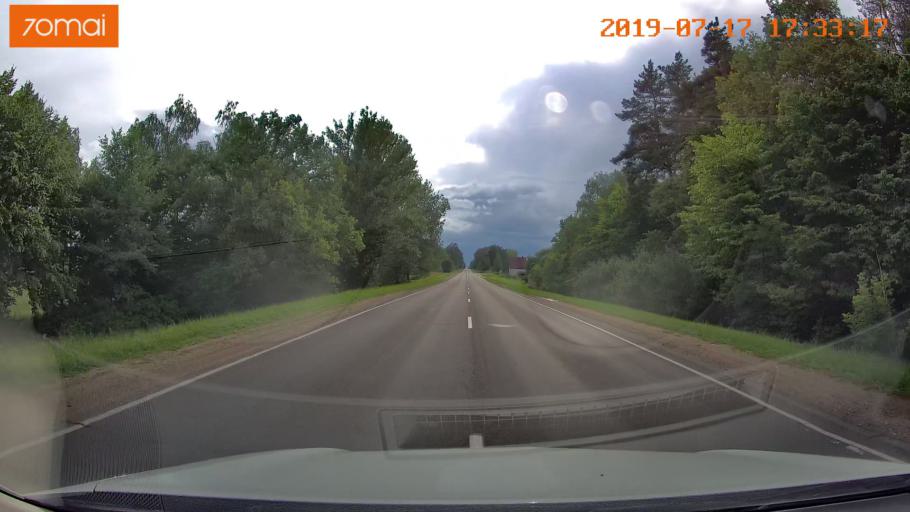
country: BY
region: Mogilev
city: Babruysk
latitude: 53.1119
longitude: 29.0957
